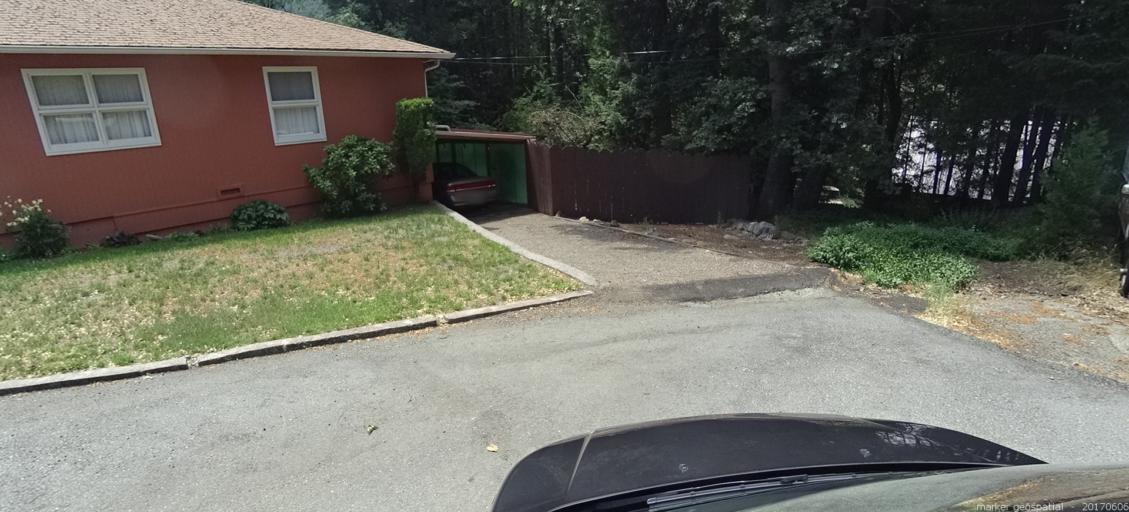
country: US
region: California
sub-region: Siskiyou County
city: Dunsmuir
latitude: 41.2357
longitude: -122.2742
